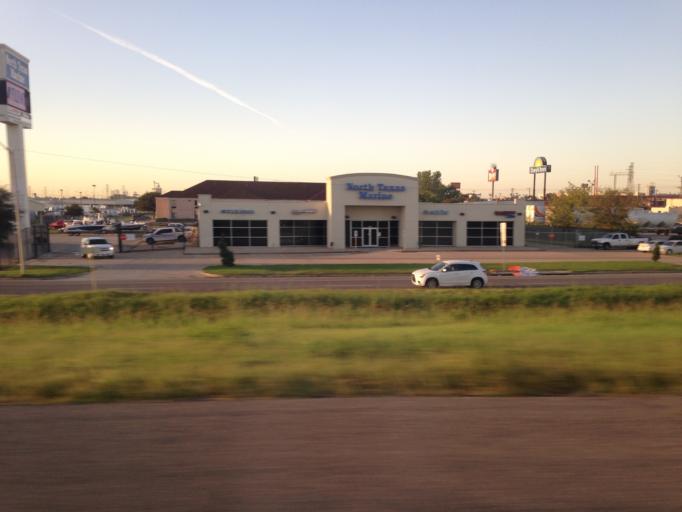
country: US
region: Texas
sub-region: Tarrant County
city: Blue Mound
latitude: 32.8427
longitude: -97.3414
